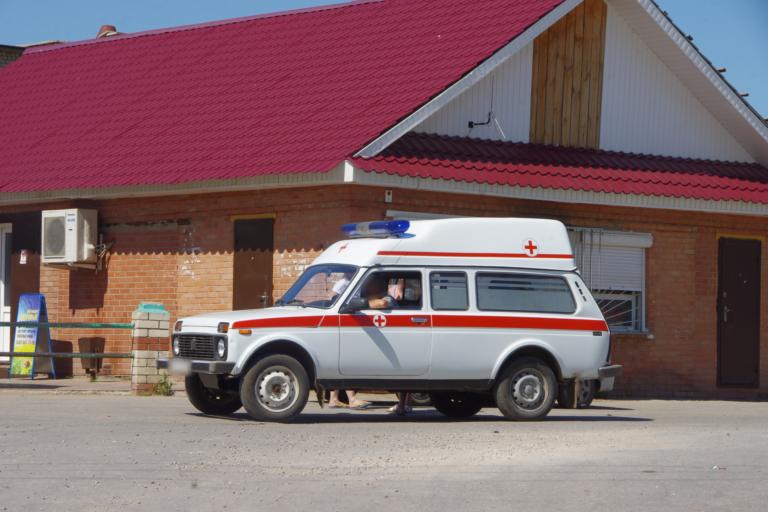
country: RU
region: Samara
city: Rozhdestveno
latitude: 53.2286
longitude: 50.0598
